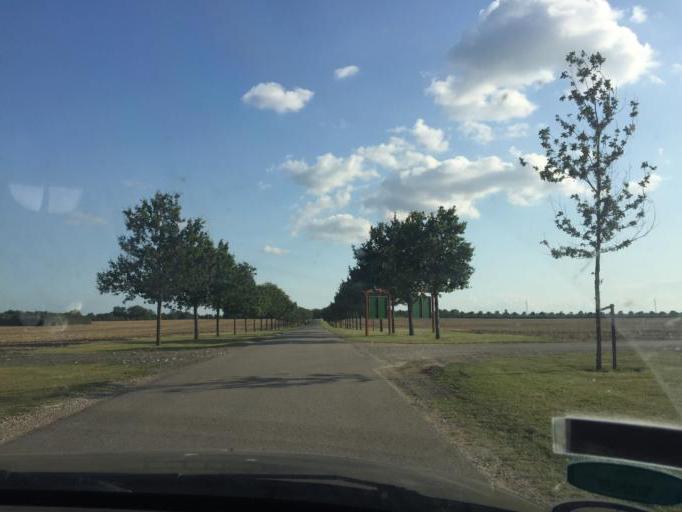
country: DK
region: Zealand
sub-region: Lolland Kommune
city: Maribo
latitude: 54.8062
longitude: 11.5090
